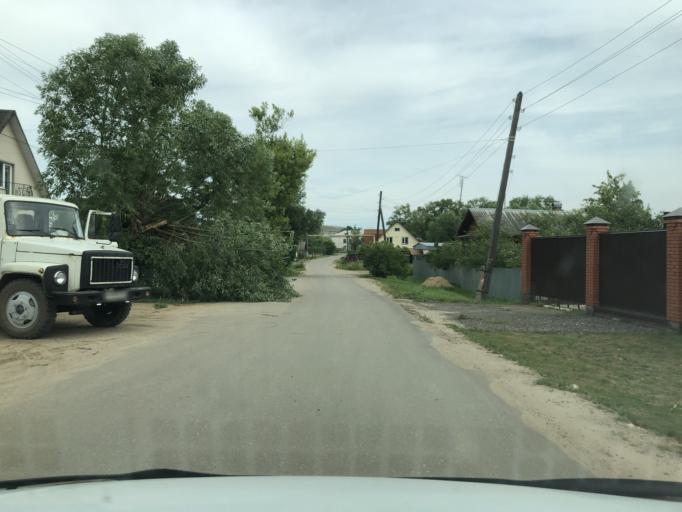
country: RU
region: Jaroslavl
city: Petrovsk
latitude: 57.0065
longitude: 39.2675
